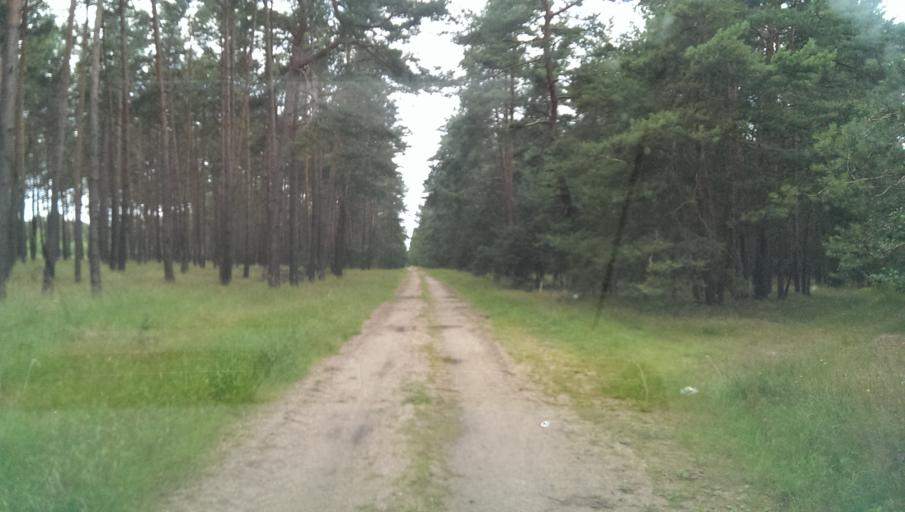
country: DE
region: Brandenburg
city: Linthe
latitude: 52.1525
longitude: 12.7719
